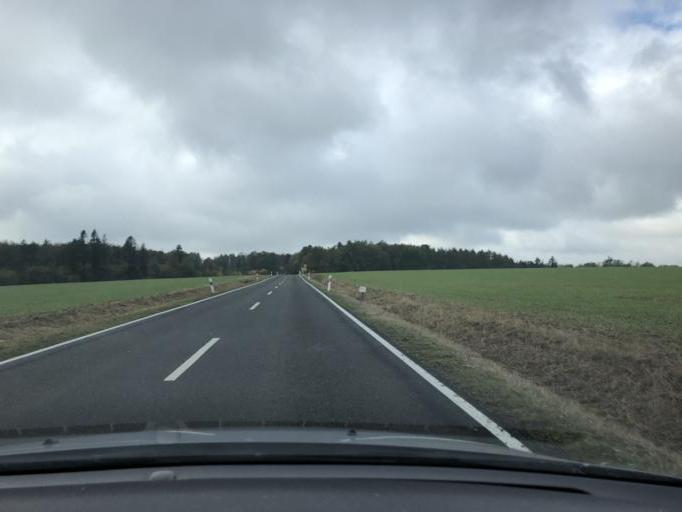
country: DE
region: Thuringia
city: Wachstedt
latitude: 51.2904
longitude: 10.2385
